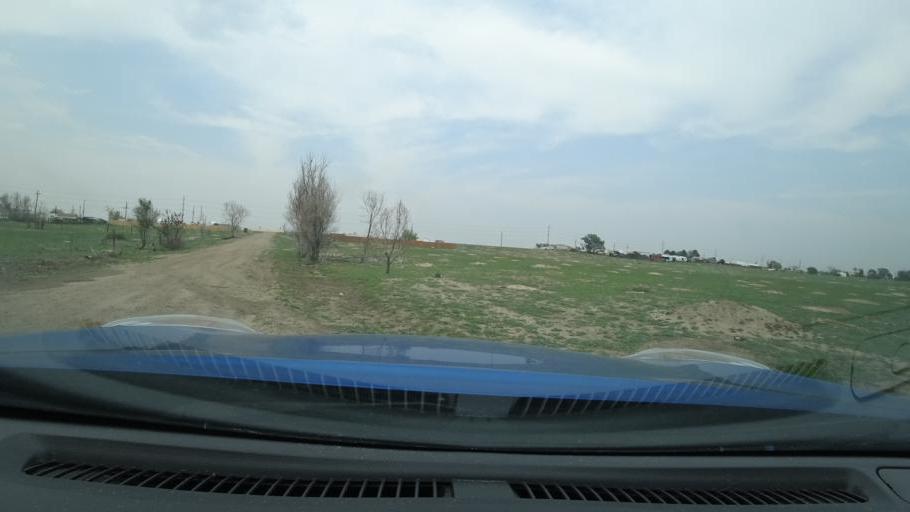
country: US
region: Colorado
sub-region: Adams County
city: Aurora
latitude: 39.7513
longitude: -104.7691
